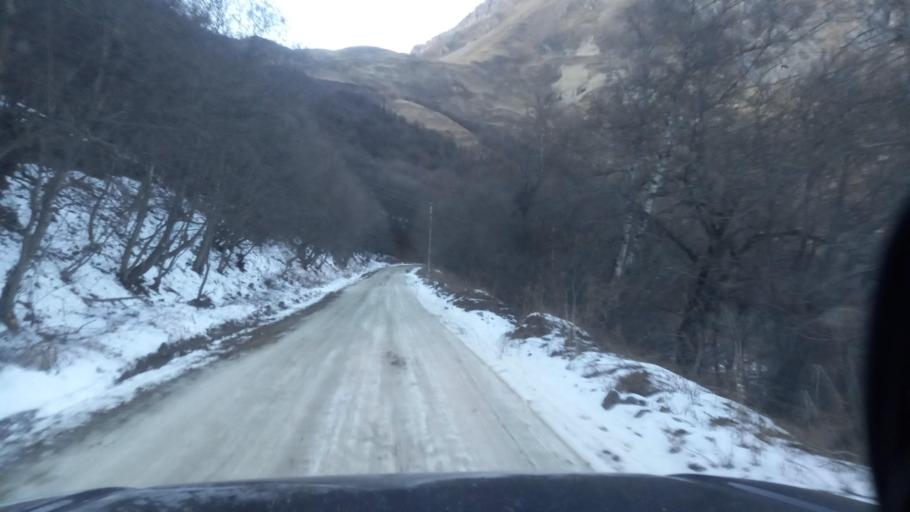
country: RU
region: Ingushetiya
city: Dzhayrakh
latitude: 42.8287
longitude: 44.5742
